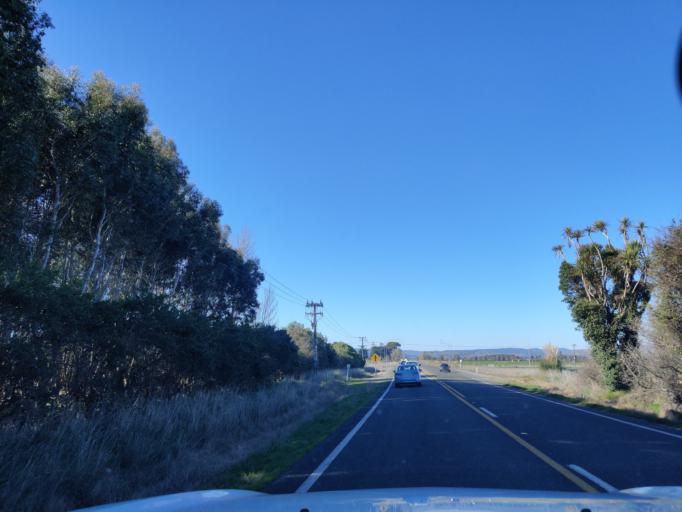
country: NZ
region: Manawatu-Wanganui
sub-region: Palmerston North City
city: Palmerston North
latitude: -40.2940
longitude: 175.5718
